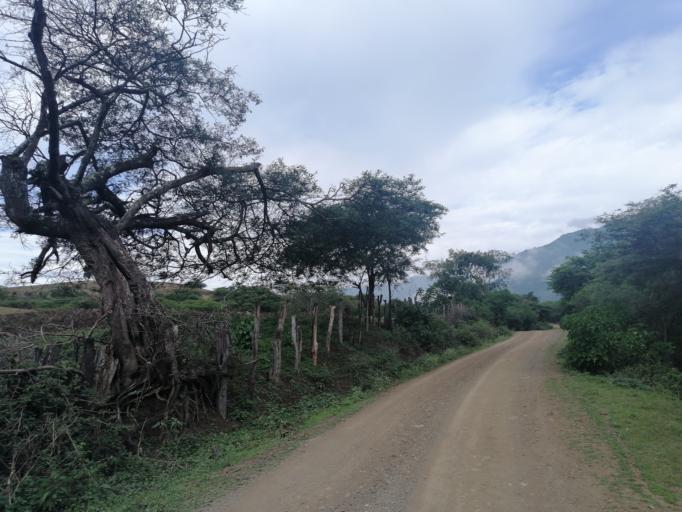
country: EC
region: Loja
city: Catacocha
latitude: -4.0122
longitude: -79.6894
